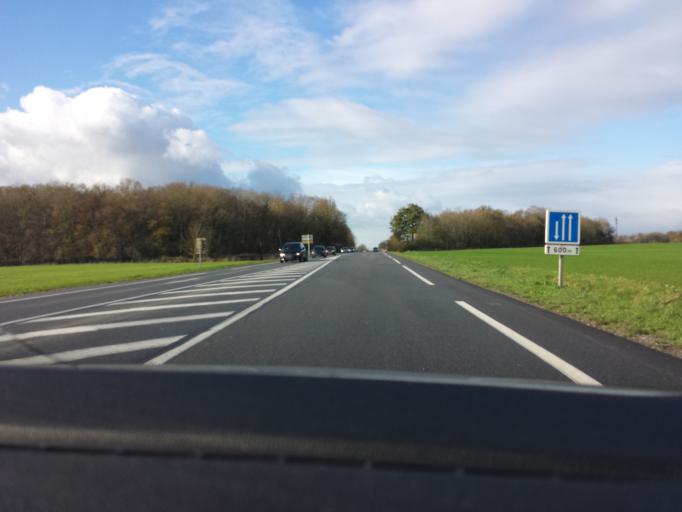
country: FR
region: Haute-Normandie
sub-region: Departement de l'Eure
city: Gravigny
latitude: 49.0136
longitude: 1.2589
